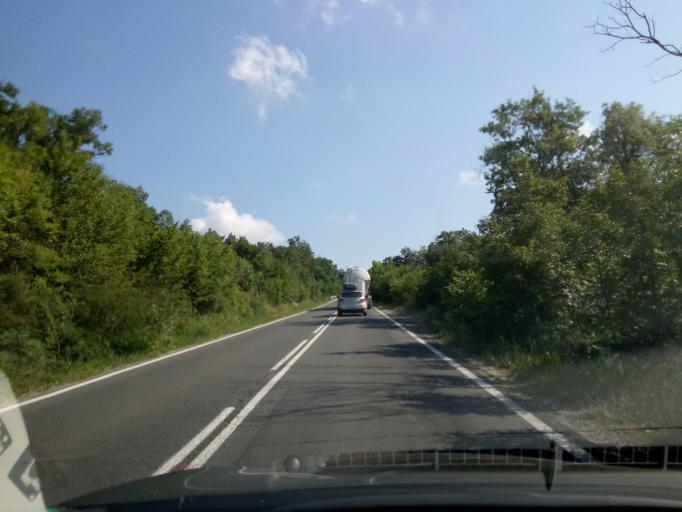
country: BG
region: Burgas
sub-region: Obshtina Nesebur
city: Sveti Vlas
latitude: 42.7430
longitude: 27.7393
